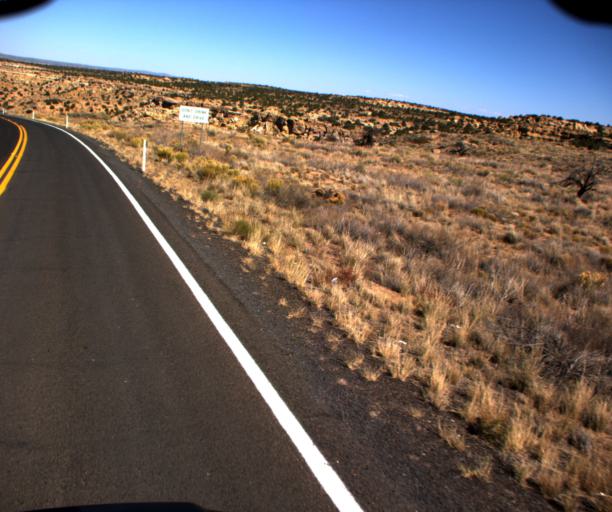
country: US
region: Arizona
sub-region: Navajo County
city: First Mesa
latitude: 35.9273
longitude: -110.6607
